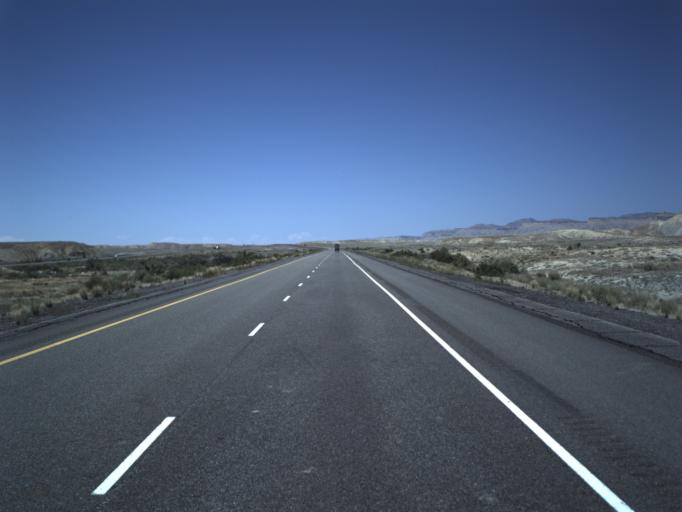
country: US
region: Utah
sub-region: Grand County
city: Moab
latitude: 38.9411
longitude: -109.5127
